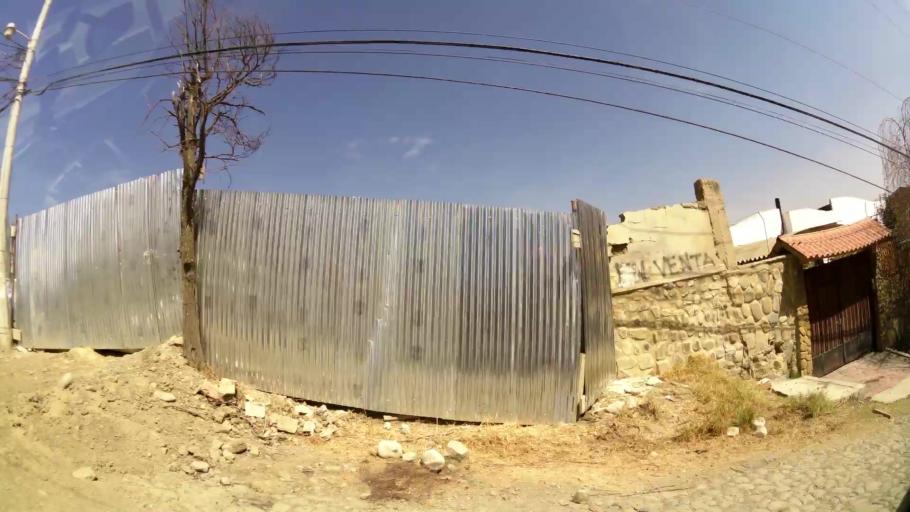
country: BO
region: La Paz
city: La Paz
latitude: -16.5413
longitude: -68.0700
